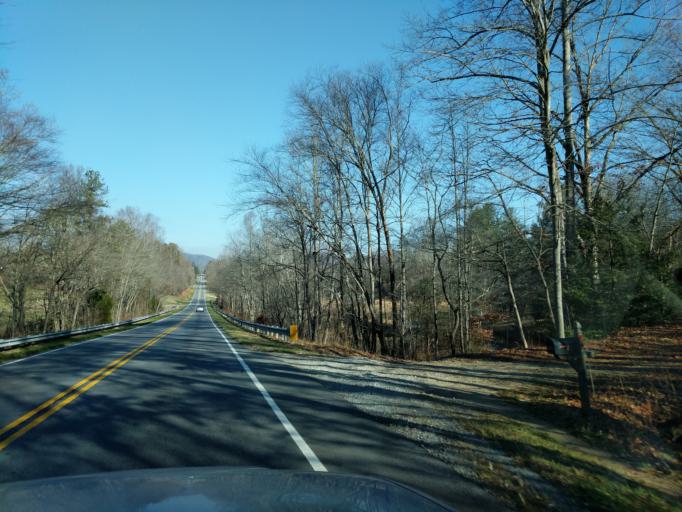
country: US
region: North Carolina
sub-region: McDowell County
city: West Marion
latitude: 35.6032
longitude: -81.9844
